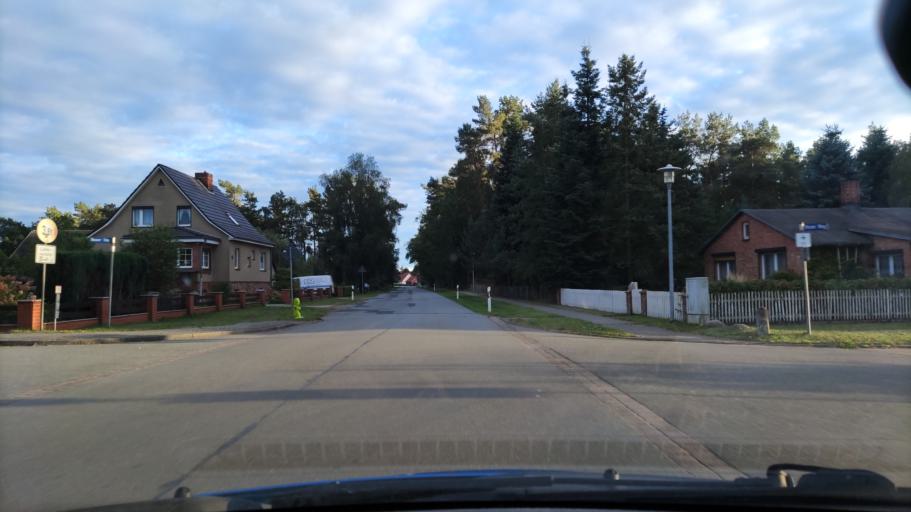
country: DE
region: Mecklenburg-Vorpommern
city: Boizenburg
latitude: 53.3736
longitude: 10.8567
